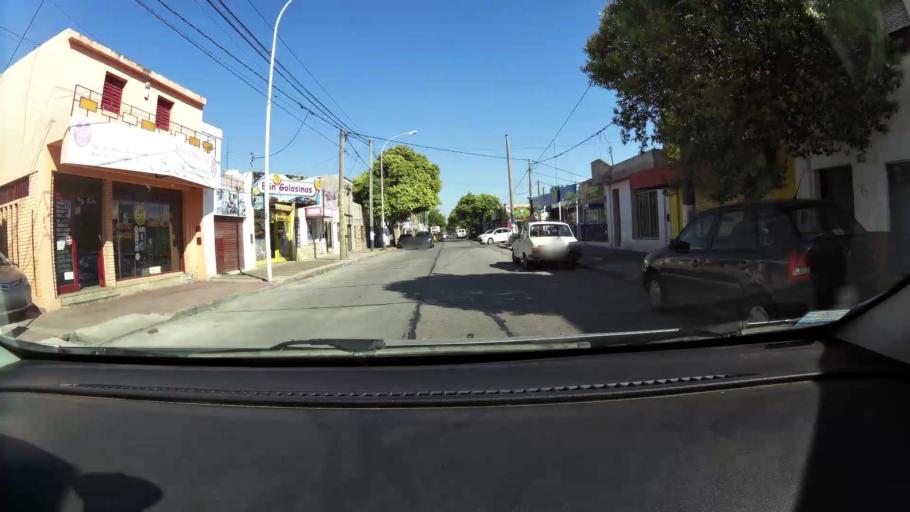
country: AR
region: Cordoba
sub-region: Departamento de Capital
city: Cordoba
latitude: -31.4375
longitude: -64.1649
